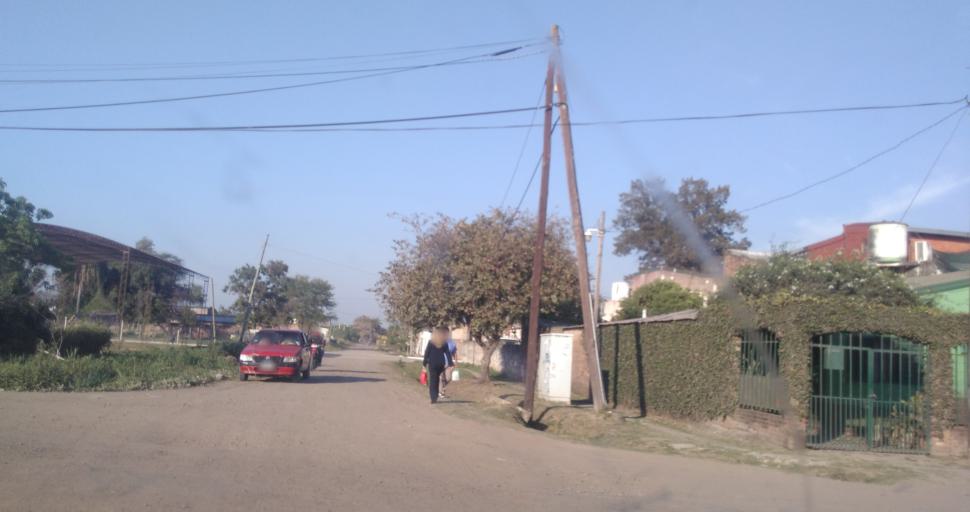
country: AR
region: Chaco
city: Fontana
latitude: -27.4142
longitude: -59.0344
